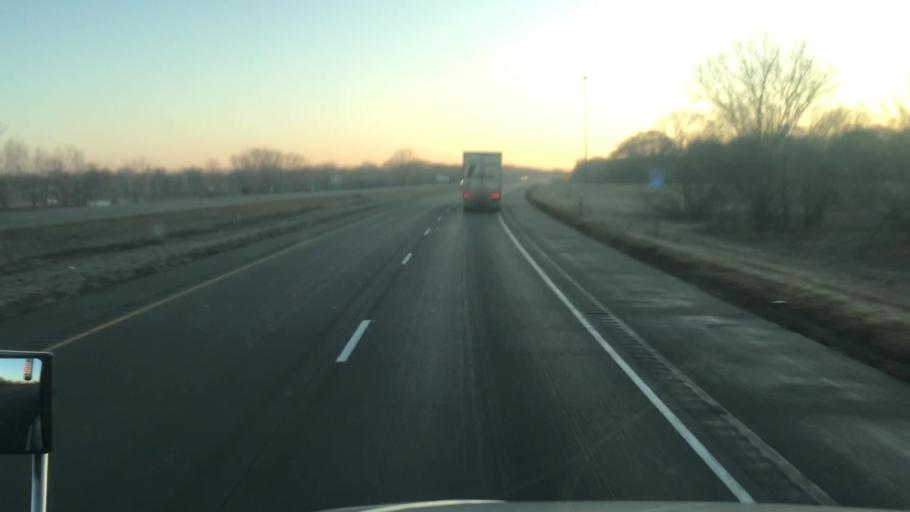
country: US
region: Iowa
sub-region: Black Hawk County
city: Evansdale
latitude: 42.4593
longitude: -92.2955
